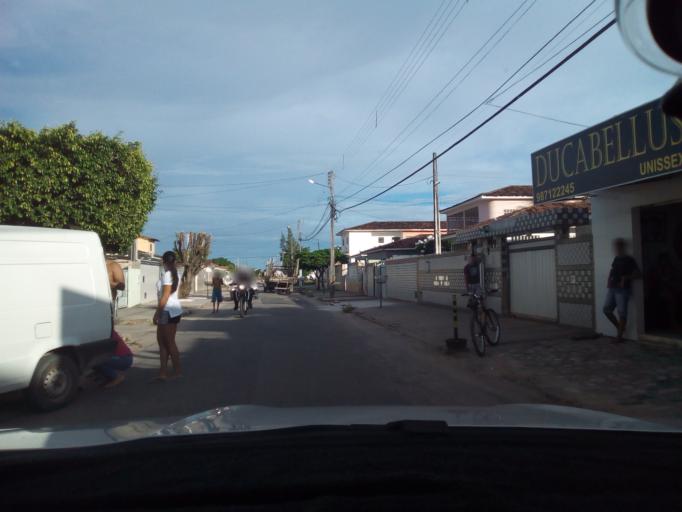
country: BR
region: Paraiba
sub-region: Joao Pessoa
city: Joao Pessoa
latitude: -7.1732
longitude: -34.8579
